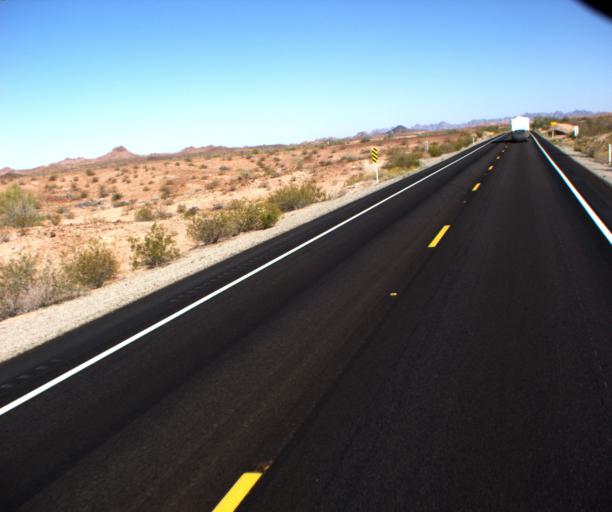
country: US
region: Arizona
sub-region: Yuma County
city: Wellton
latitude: 33.0635
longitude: -114.2931
